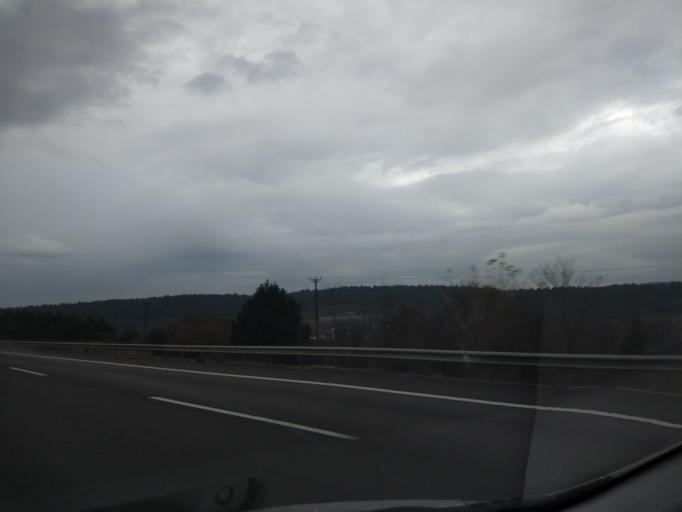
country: TR
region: Bolu
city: Yenicaga
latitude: 40.7528
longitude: 31.9253
